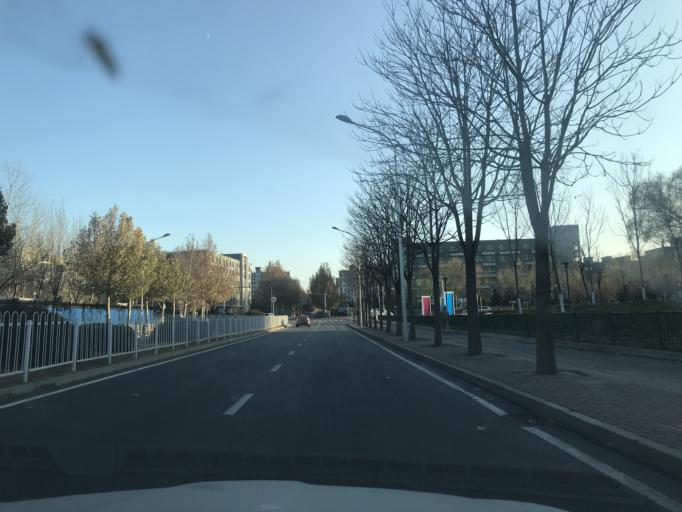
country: CN
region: Beijing
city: Xibeiwang
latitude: 40.0689
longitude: 116.2471
